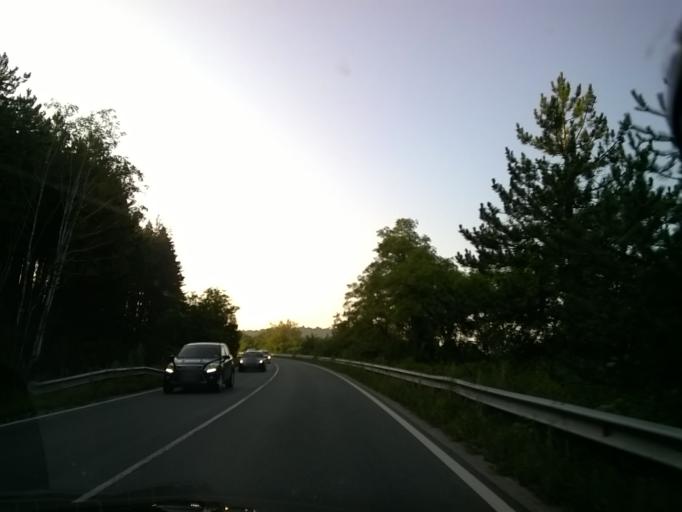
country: BG
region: Sofiya
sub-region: Obshtina Dragoman
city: Dragoman
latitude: 42.9400
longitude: 22.9052
